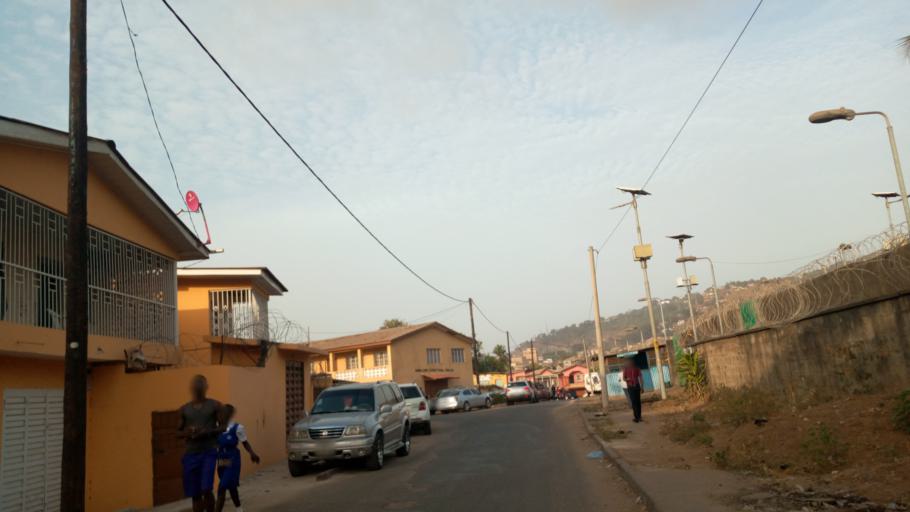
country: SL
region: Western Area
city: Freetown
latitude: 8.4727
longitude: -13.2413
